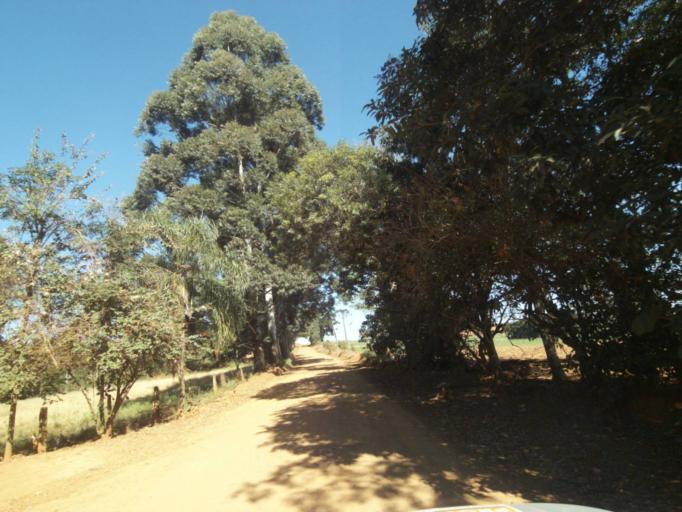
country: BR
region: Parana
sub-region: Tibagi
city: Tibagi
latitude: -24.5566
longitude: -50.6215
